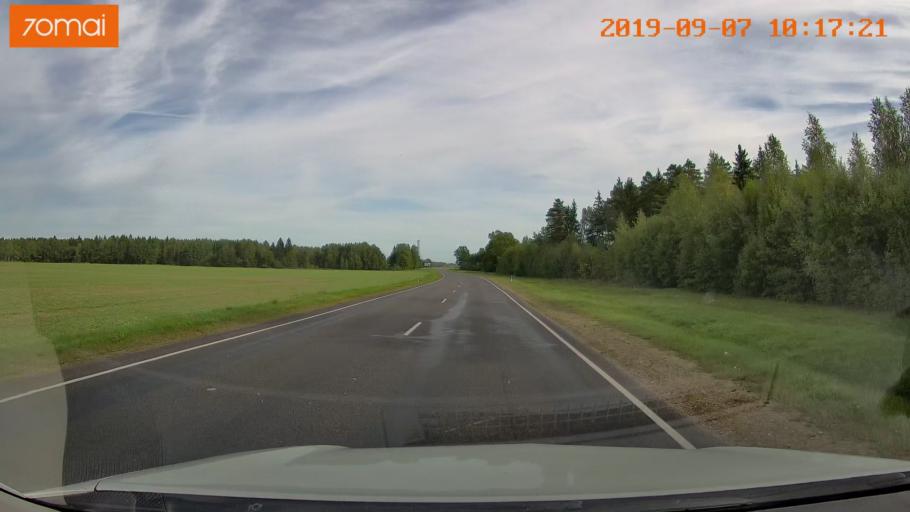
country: BY
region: Grodnenskaya
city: Voranava
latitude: 54.1712
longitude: 25.3333
